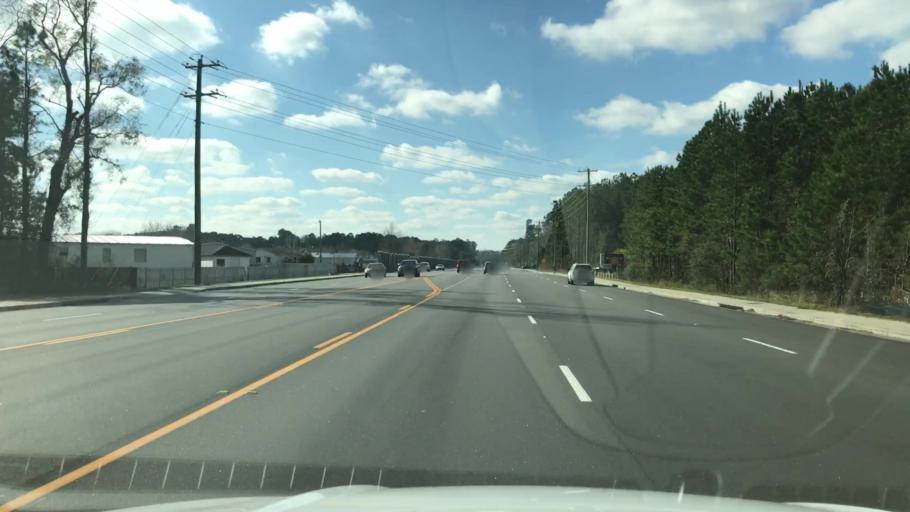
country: US
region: South Carolina
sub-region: Horry County
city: Socastee
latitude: 33.6475
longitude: -79.0245
